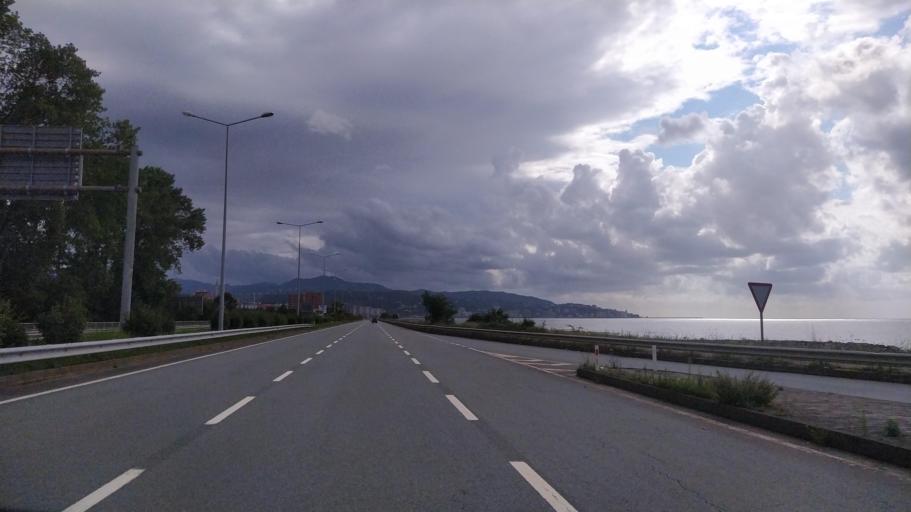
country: TR
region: Rize
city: Ardesen
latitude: 41.1875
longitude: 40.9582
